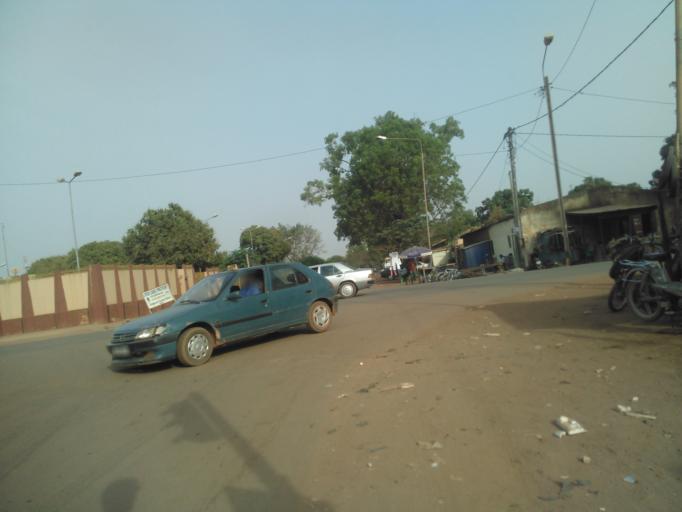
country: BF
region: High-Basins
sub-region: Province du Houet
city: Bobo-Dioulasso
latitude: 11.1740
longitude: -4.3066
